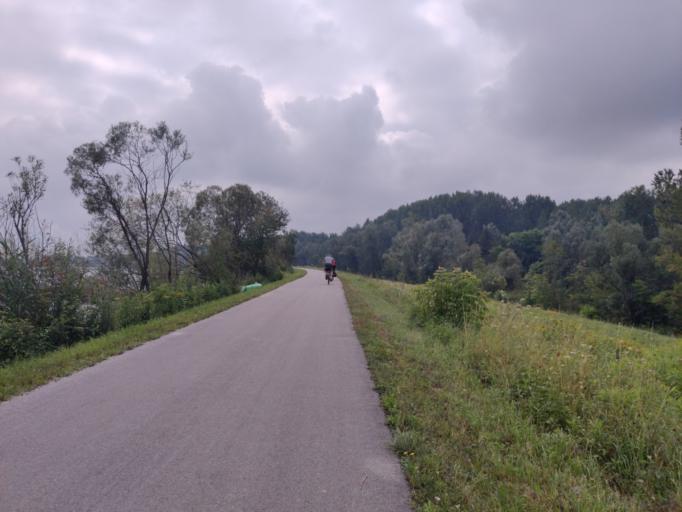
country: AT
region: Lower Austria
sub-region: Politischer Bezirk Sankt Polten
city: Traismauer
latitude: 48.3719
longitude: 15.7383
